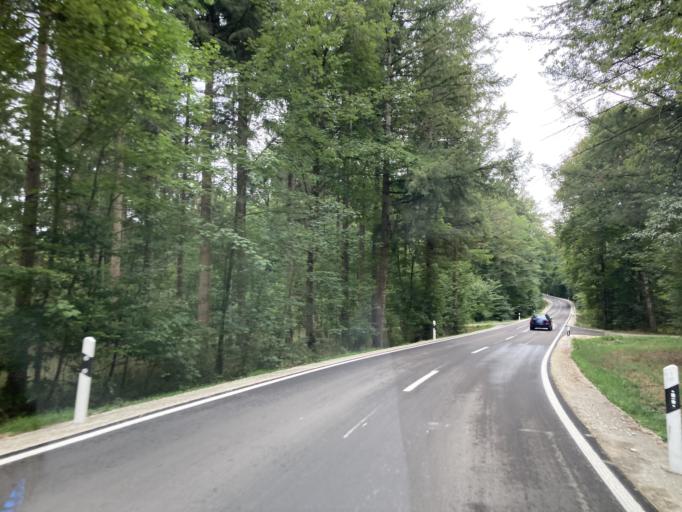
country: DE
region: Bavaria
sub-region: Swabia
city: Forheim
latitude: 48.8016
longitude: 10.4118
